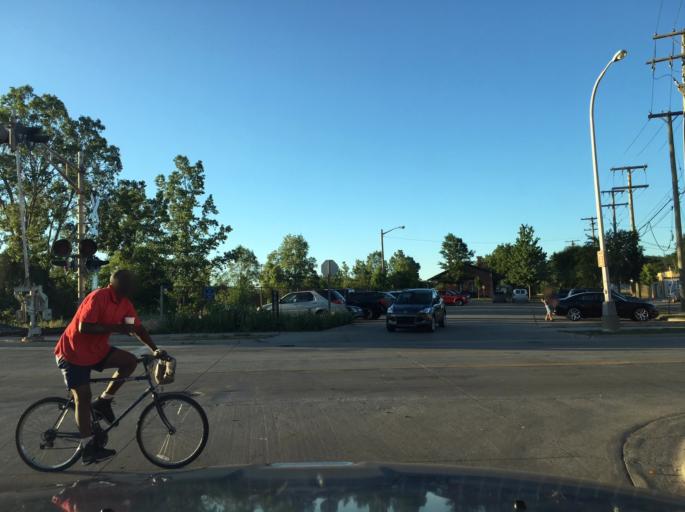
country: US
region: Michigan
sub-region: Macomb County
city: Mount Clemens
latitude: 42.5981
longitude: -82.8927
